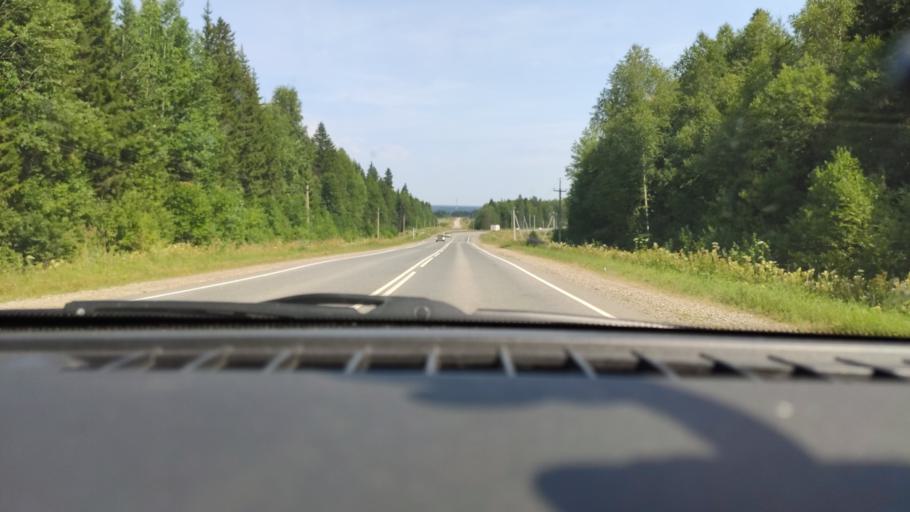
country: RU
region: Perm
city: Kukushtan
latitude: 57.6289
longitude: 56.4300
